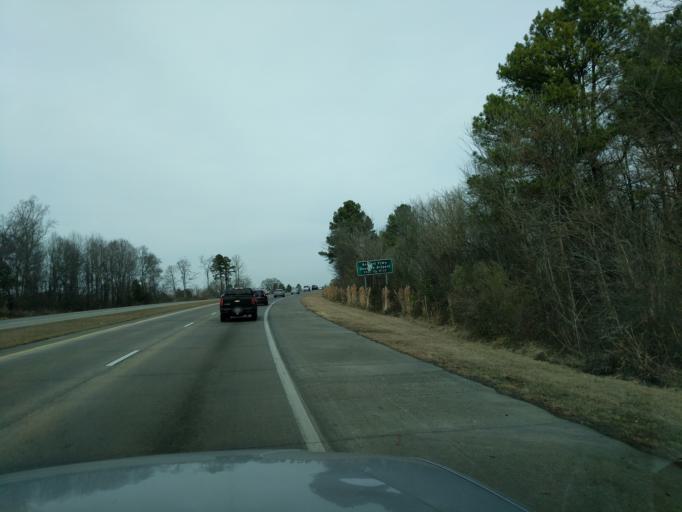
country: US
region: North Carolina
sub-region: Mecklenburg County
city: Charlotte
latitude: 35.2098
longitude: -80.9234
